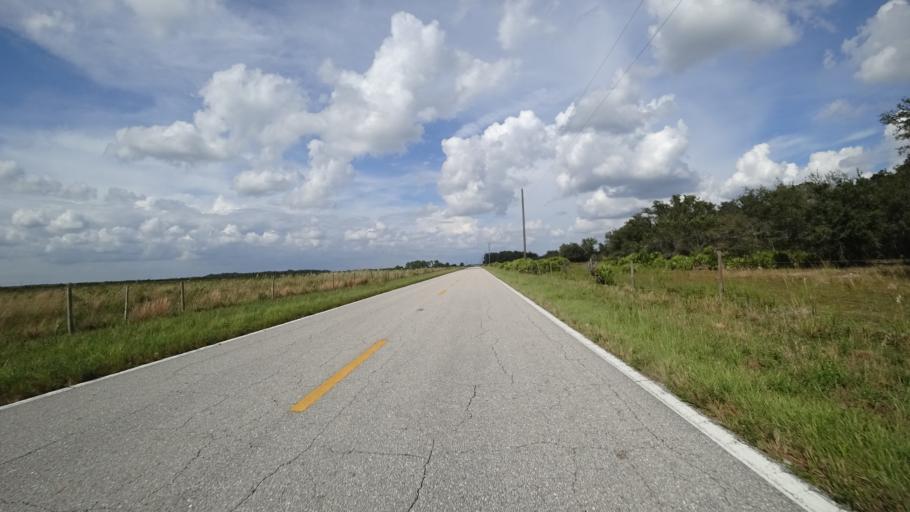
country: US
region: Florida
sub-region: Hardee County
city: Wauchula
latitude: 27.5085
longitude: -82.0719
